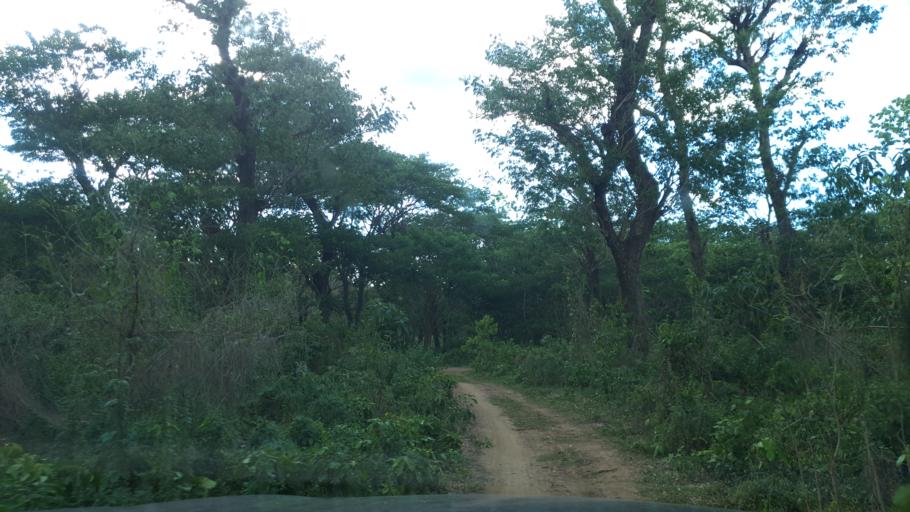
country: TH
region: Lampang
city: Sop Prap
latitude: 17.8846
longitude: 99.2908
